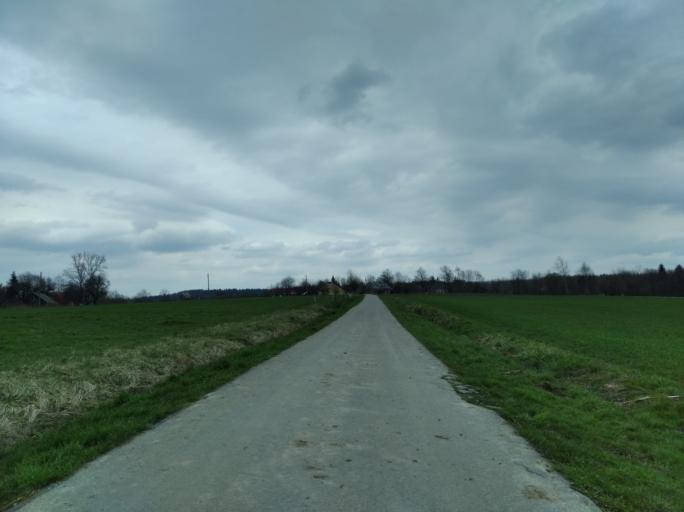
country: PL
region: Subcarpathian Voivodeship
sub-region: Powiat strzyzowski
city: Wysoka Strzyzowska
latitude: 49.8074
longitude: 21.7742
